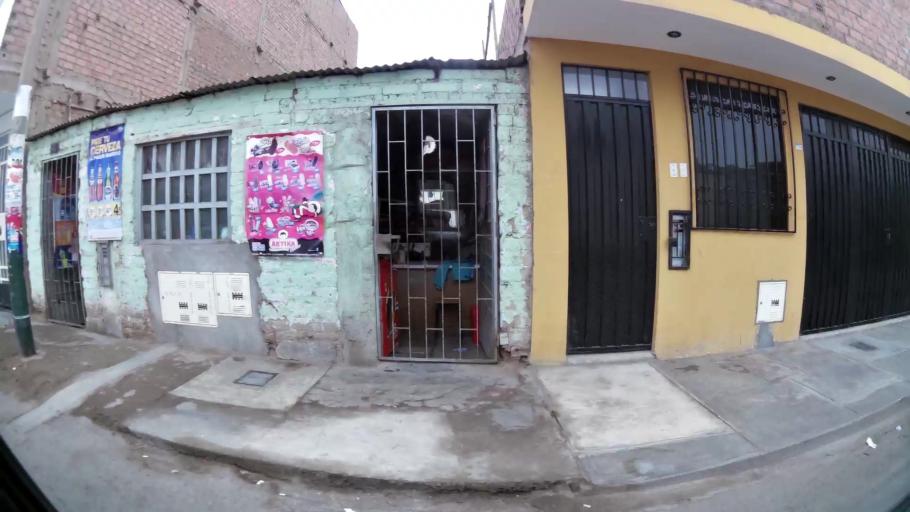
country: PE
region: Lima
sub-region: Lima
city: Independencia
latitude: -11.9546
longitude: -77.0829
